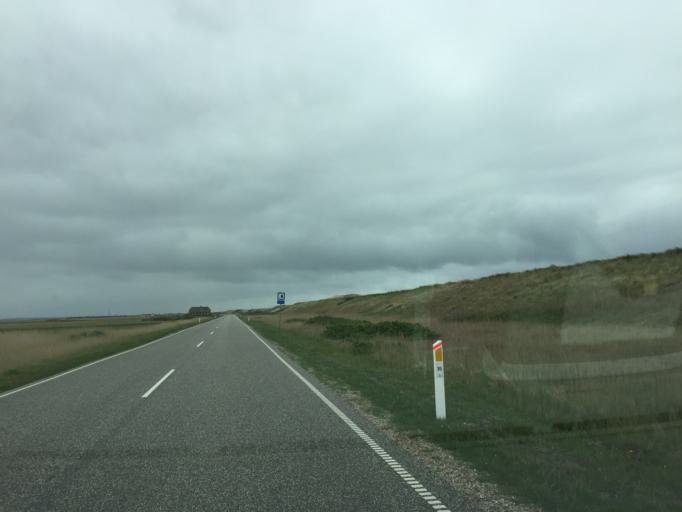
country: DK
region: Central Jutland
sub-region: Lemvig Kommune
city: Harboore
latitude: 56.3993
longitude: 8.1216
